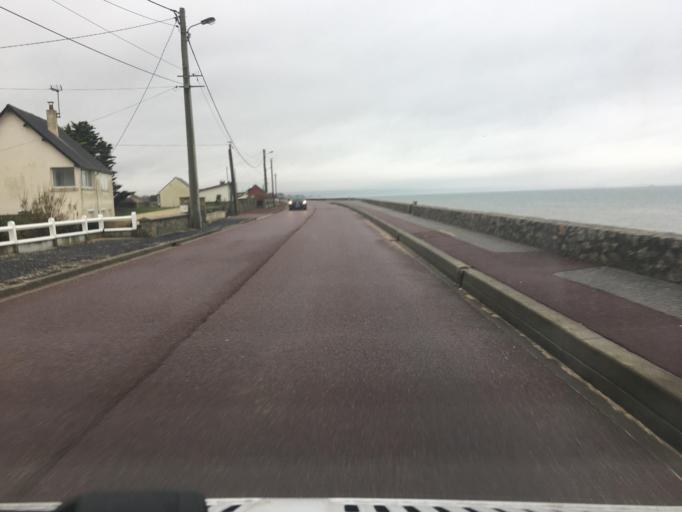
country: FR
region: Lower Normandy
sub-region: Departement de la Manche
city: Saint-Vaast-la-Hougue
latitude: 49.4997
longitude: -1.2694
